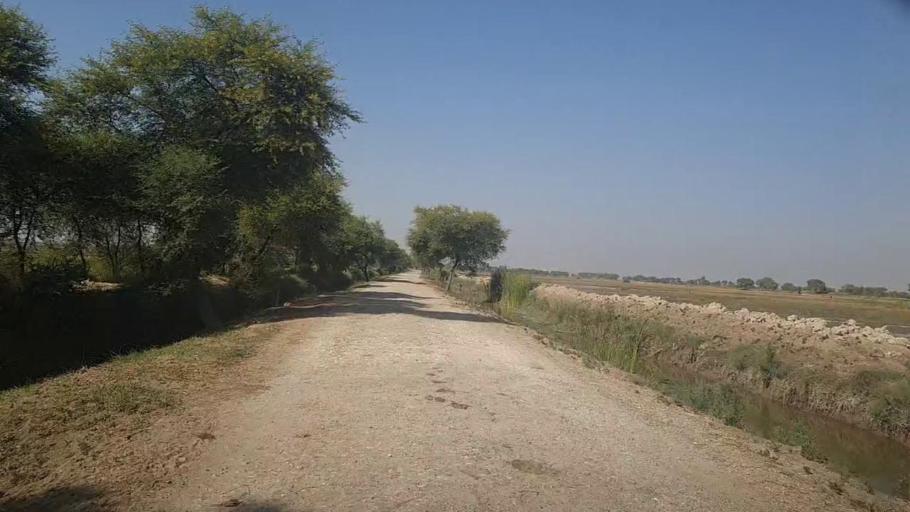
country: PK
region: Sindh
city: Thul
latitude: 28.3062
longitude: 68.7705
